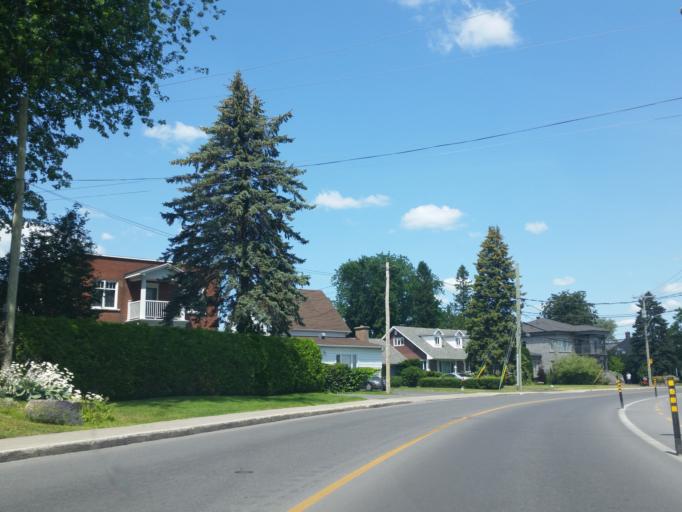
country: CA
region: Quebec
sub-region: Monteregie
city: Saint-Jean-sur-Richelieu
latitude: 45.3205
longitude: -73.2624
